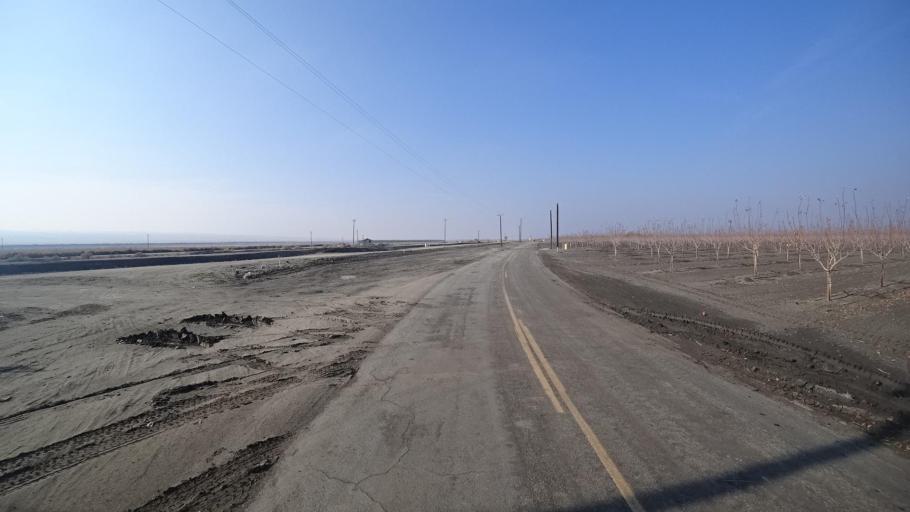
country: US
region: California
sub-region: Kern County
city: Buttonwillow
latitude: 35.3402
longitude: -119.4268
